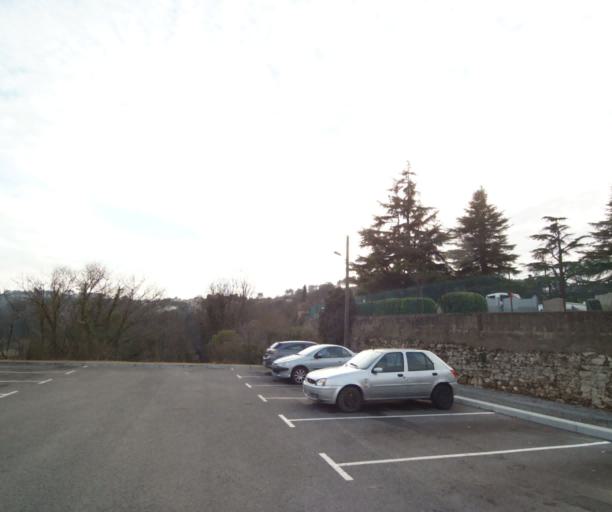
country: FR
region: Provence-Alpes-Cote d'Azur
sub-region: Departement du Var
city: Trans-en-Provence
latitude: 43.5020
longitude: 6.4880
